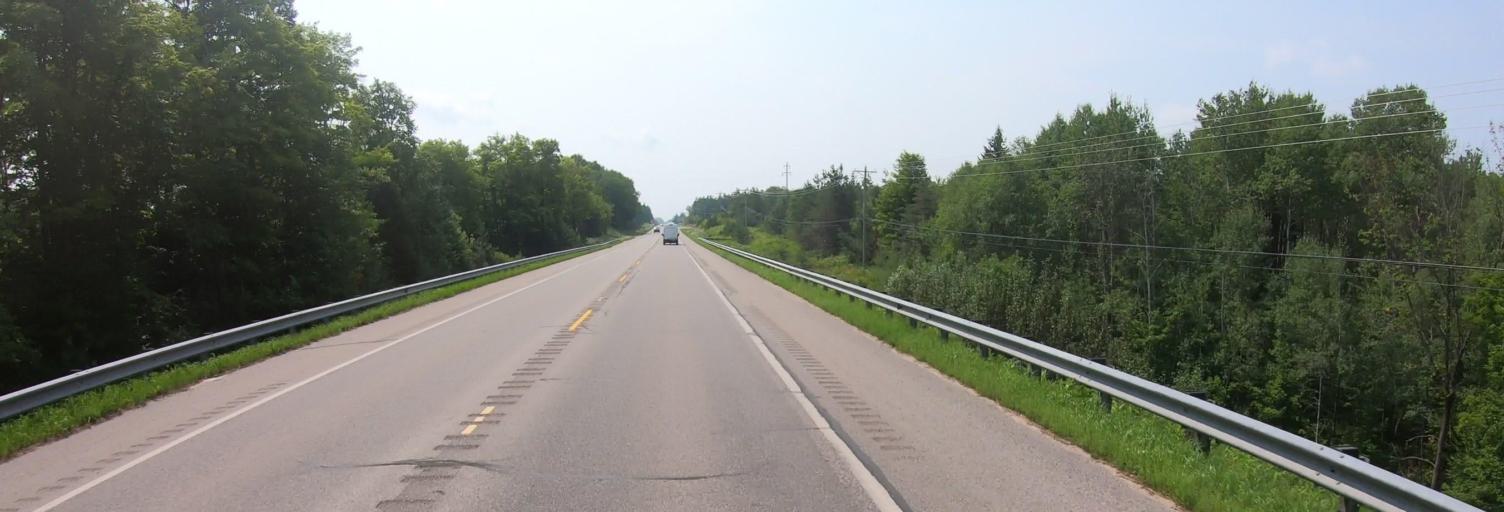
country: US
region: Michigan
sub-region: Luce County
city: Newberry
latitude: 46.3212
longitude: -85.5097
